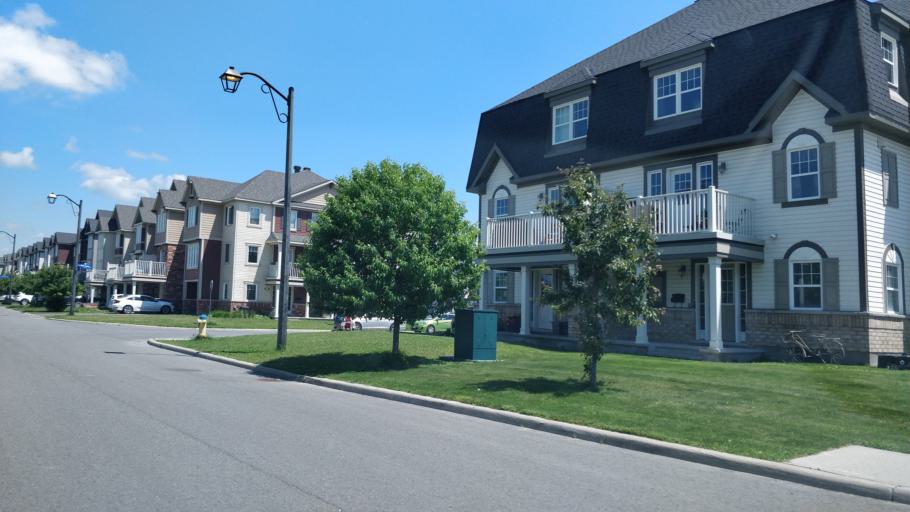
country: CA
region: Ontario
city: Bells Corners
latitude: 45.2470
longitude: -75.7356
